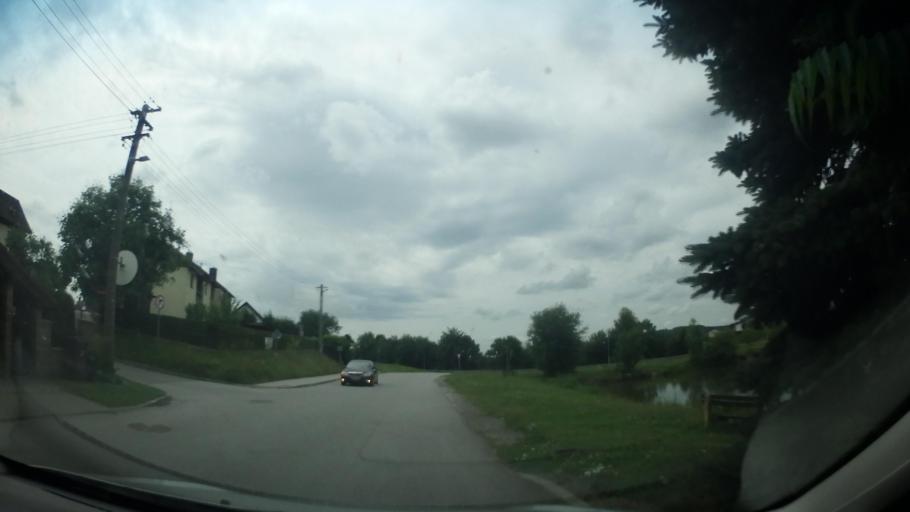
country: CZ
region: Vysocina
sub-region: Okres Zd'ar nad Sazavou
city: Nove Mesto na Morave
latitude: 49.5762
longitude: 16.0782
